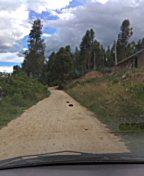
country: CO
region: Boyaca
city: Paipa
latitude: 5.8221
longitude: -73.0875
